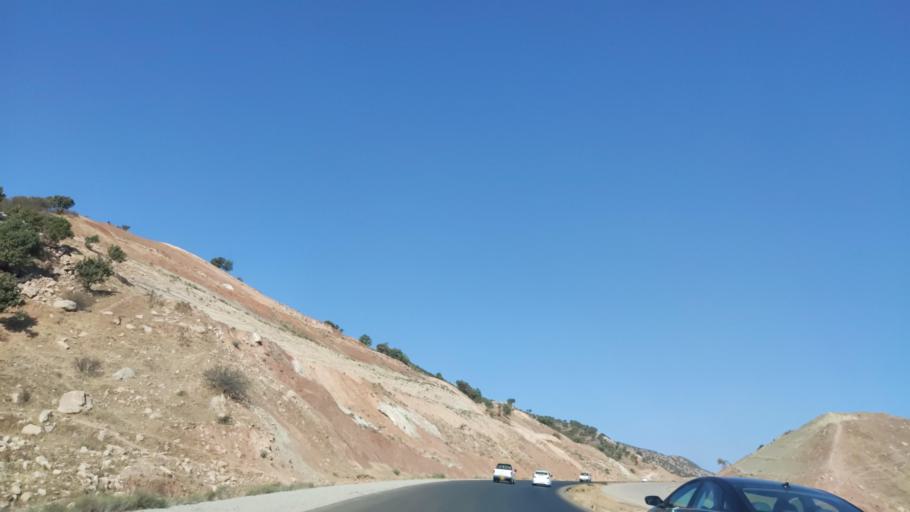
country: IQ
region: Arbil
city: Shaqlawah
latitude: 36.4351
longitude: 44.2965
